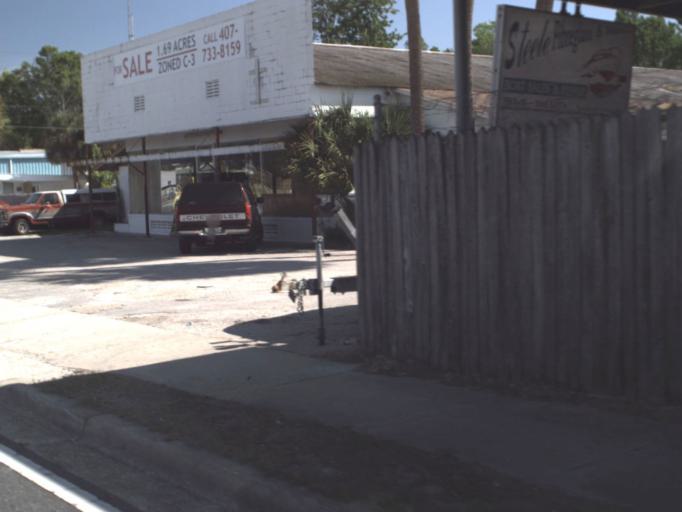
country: US
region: Florida
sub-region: Lake County
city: Leesburg
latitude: 28.7989
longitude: -81.8876
